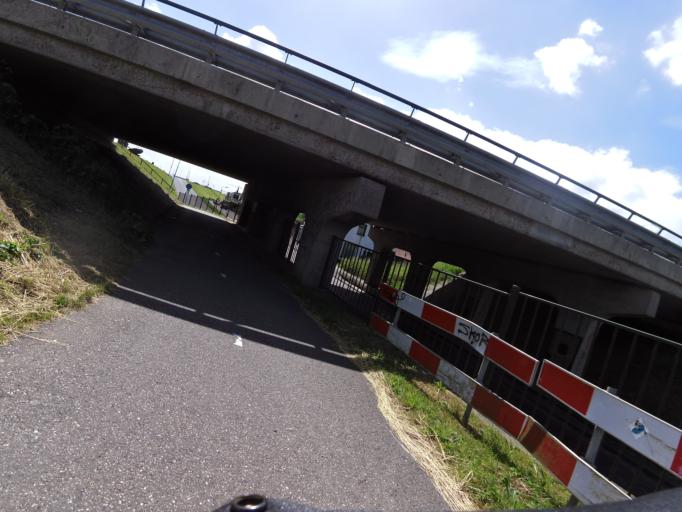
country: NL
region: Zeeland
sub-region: Schouwen-Duiveland
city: Bruinisse
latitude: 51.6662
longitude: 4.0919
